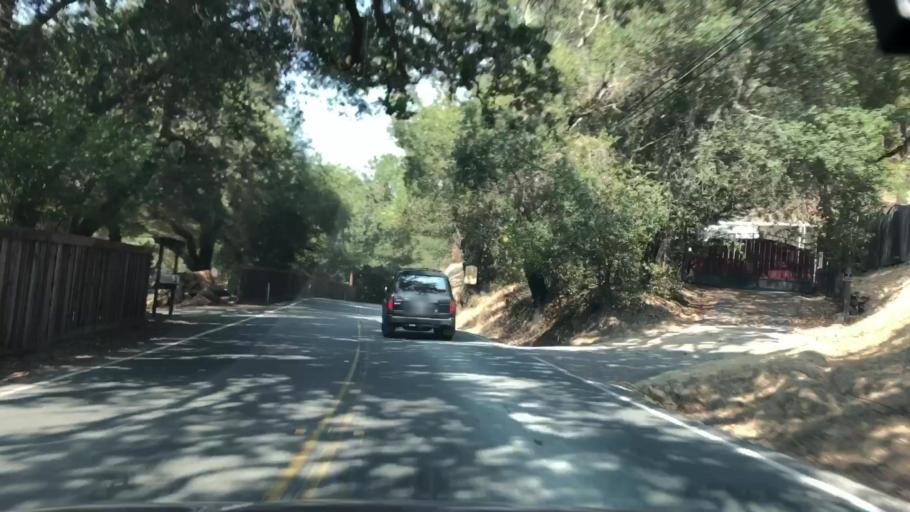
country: US
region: California
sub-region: Sonoma County
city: Larkfield-Wikiup
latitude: 38.5498
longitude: -122.7145
